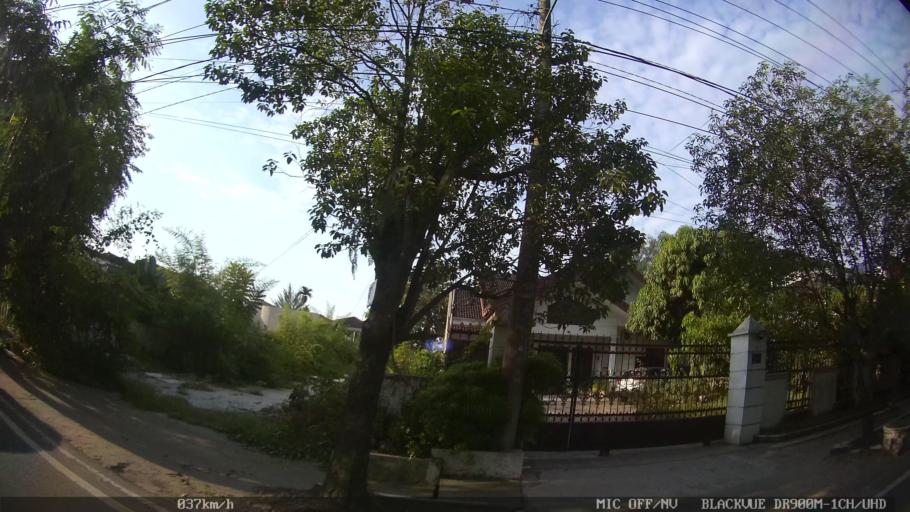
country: ID
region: North Sumatra
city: Medan
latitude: 3.5772
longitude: 98.6481
